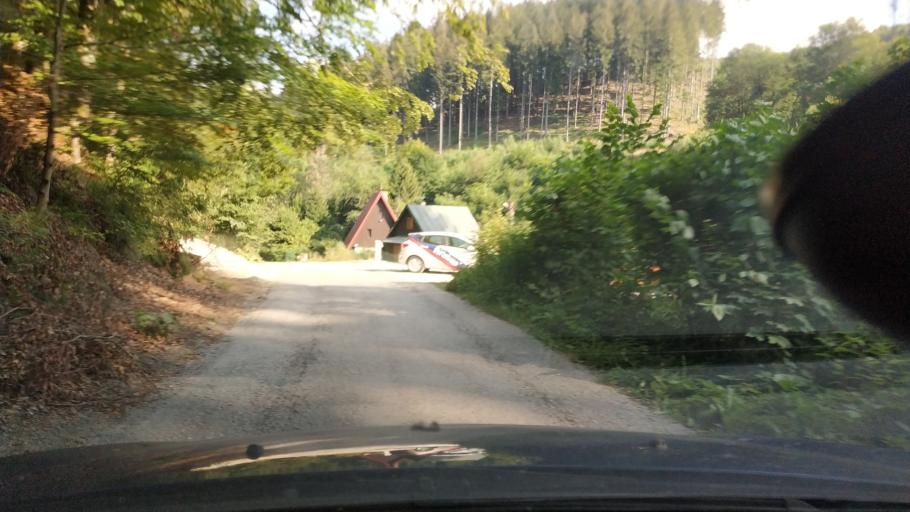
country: SK
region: Zilinsky
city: Ruzomberok
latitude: 48.9955
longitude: 19.2634
